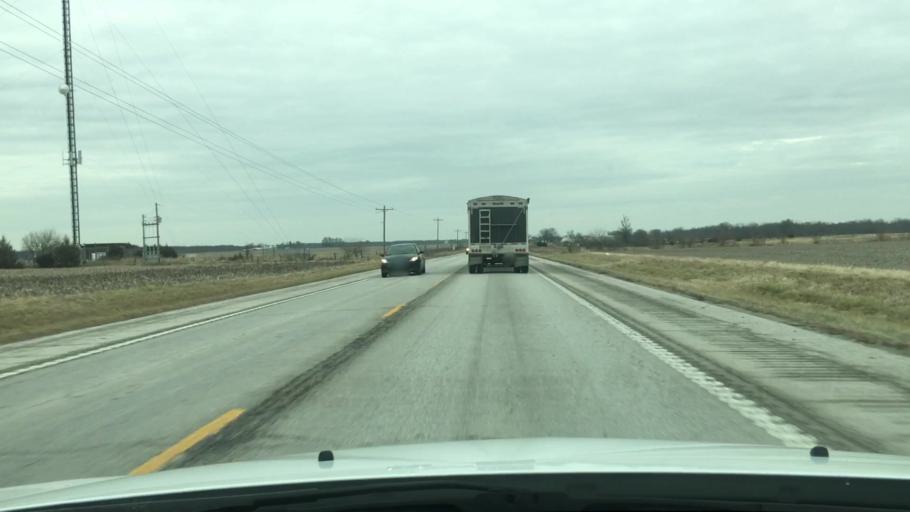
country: US
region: Missouri
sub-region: Montgomery County
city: Wellsville
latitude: 39.1692
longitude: -91.6477
